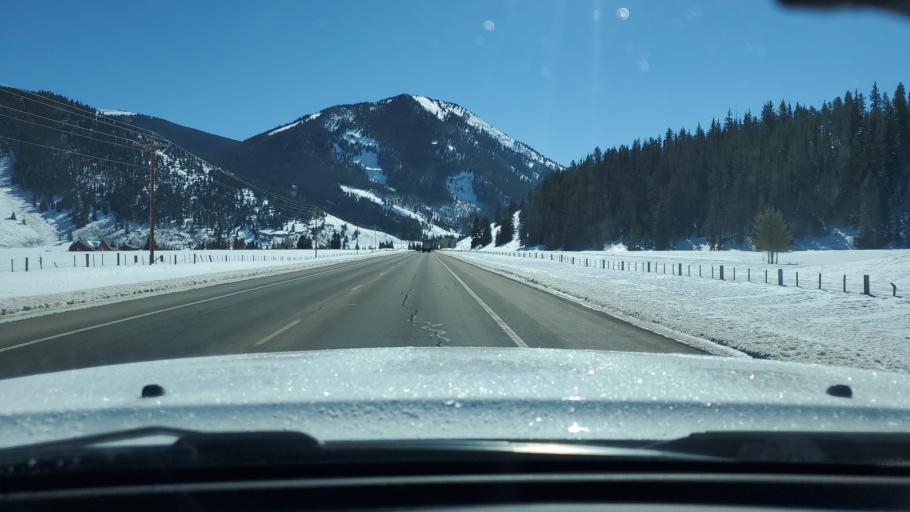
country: US
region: Colorado
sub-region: Gunnison County
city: Crested Butte
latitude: 38.8005
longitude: -106.8846
